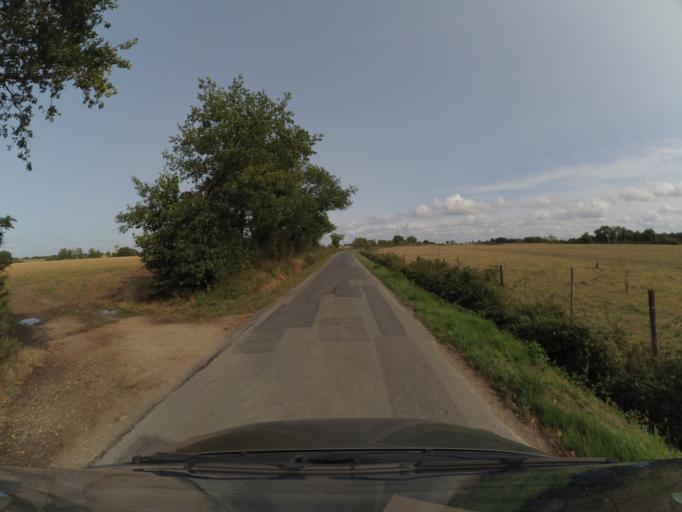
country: FR
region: Pays de la Loire
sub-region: Departement de la Vendee
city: La Bruffiere
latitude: 46.9936
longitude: -1.1921
